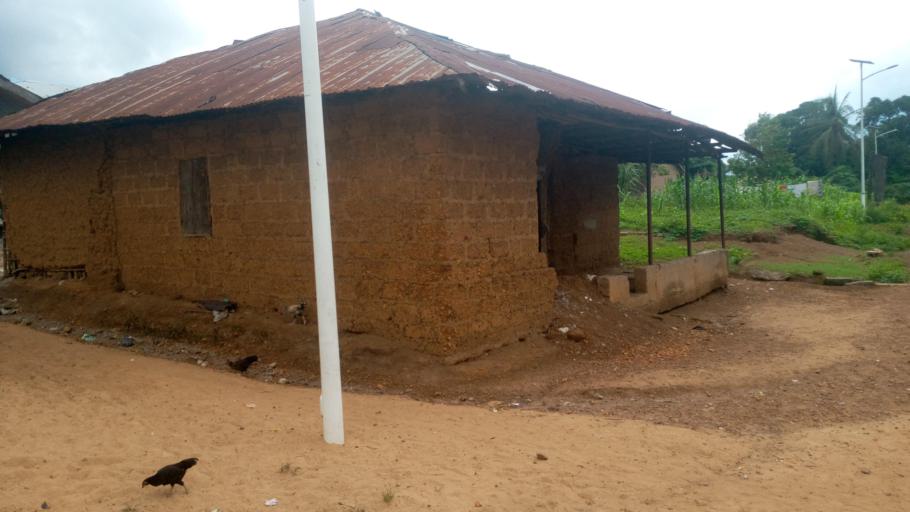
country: SL
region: Southern Province
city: Mogbwemo
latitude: 7.6048
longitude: -12.1790
